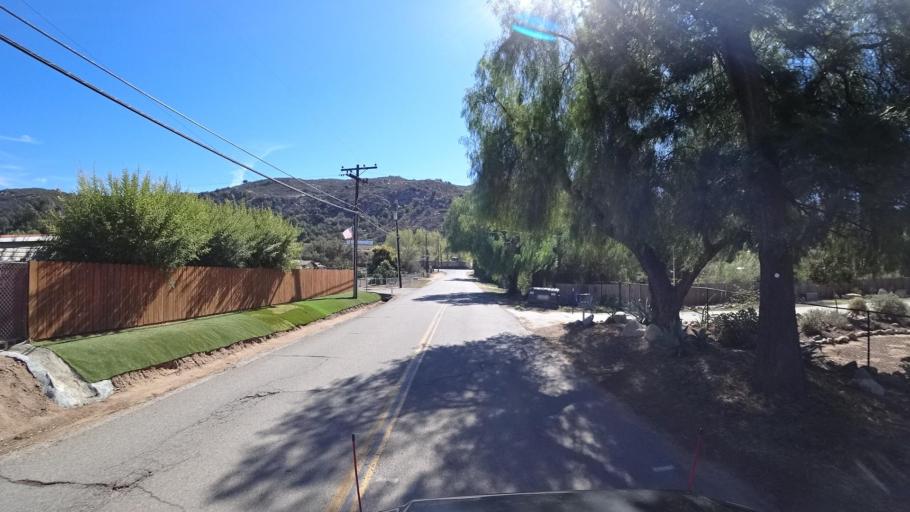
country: US
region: California
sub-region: San Diego County
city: Harbison Canyon
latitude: 32.8579
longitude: -116.8346
